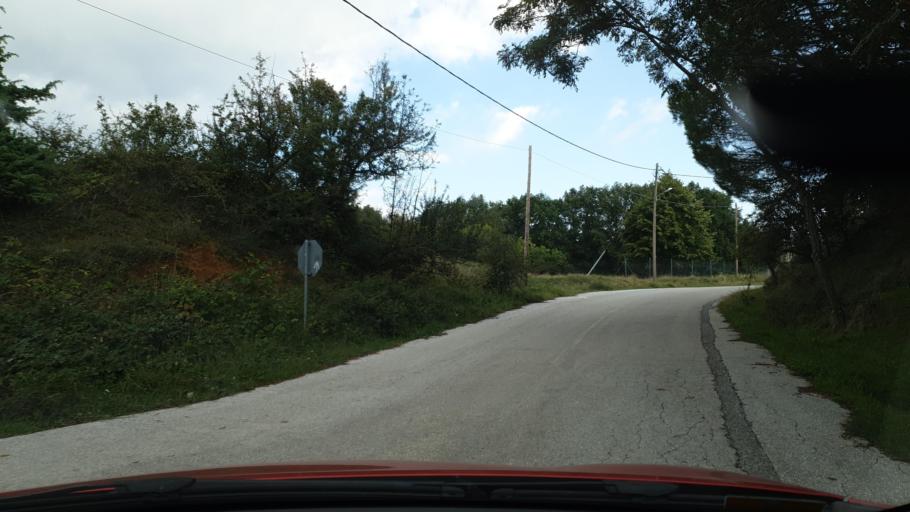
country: GR
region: Central Macedonia
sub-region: Nomos Thessalonikis
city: Peristera
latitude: 40.5203
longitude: 23.2090
